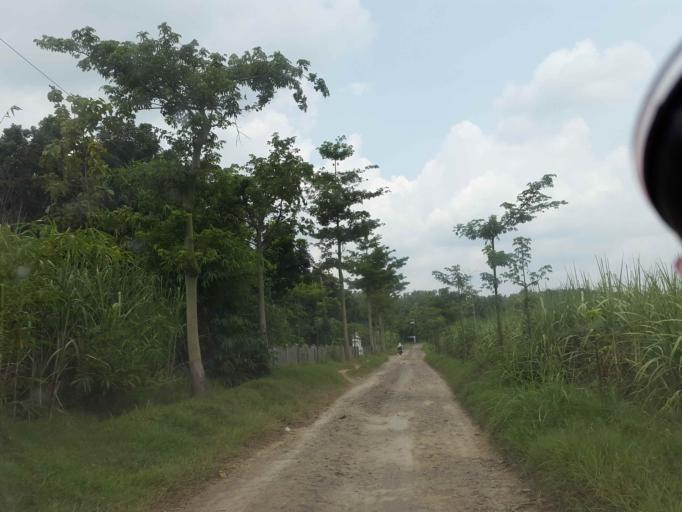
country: ID
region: Central Java
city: Pemalang
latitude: -6.9511
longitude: 109.2898
